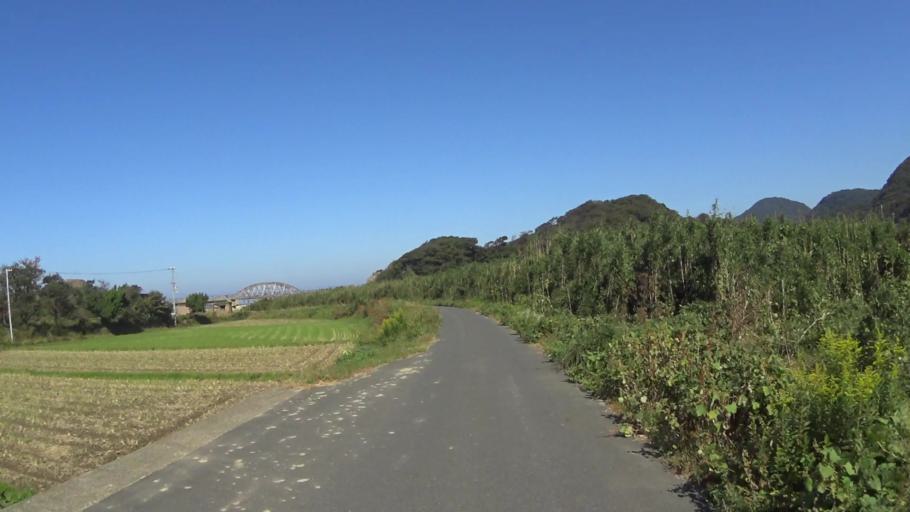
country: JP
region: Kyoto
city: Miyazu
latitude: 35.7408
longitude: 135.1051
